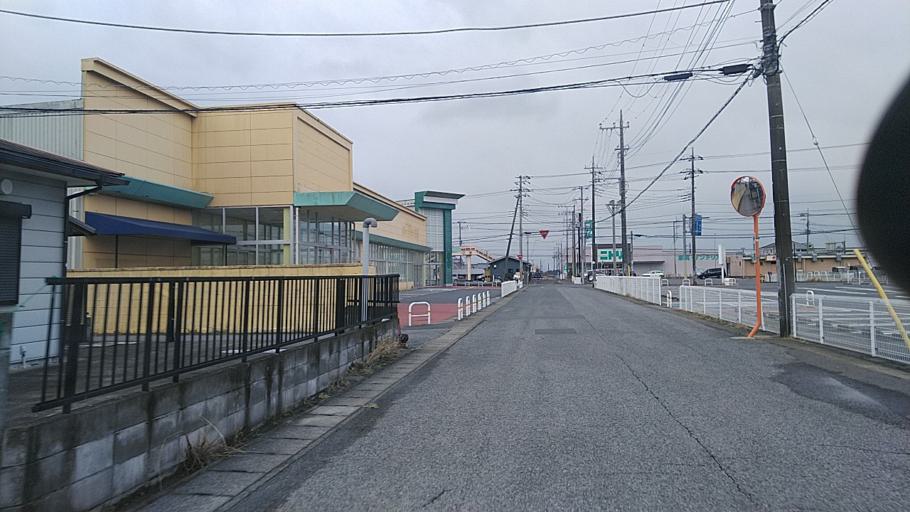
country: JP
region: Chiba
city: Togane
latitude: 35.5768
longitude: 140.3801
